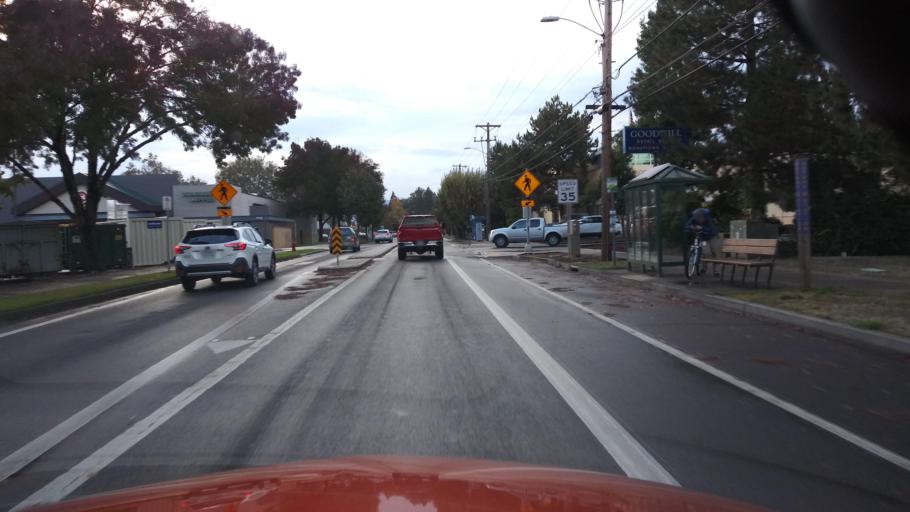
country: US
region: Oregon
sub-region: Washington County
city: Forest Grove
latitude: 45.5202
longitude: -123.0941
